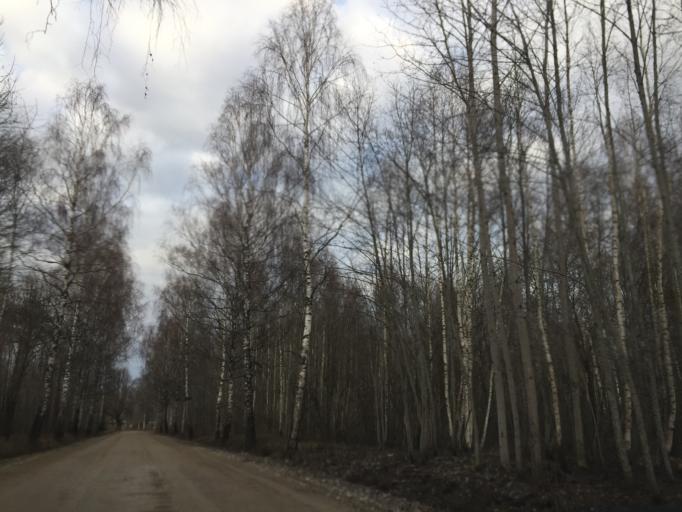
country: LV
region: Jaunjelgava
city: Jaunjelgava
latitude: 56.6014
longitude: 25.0619
